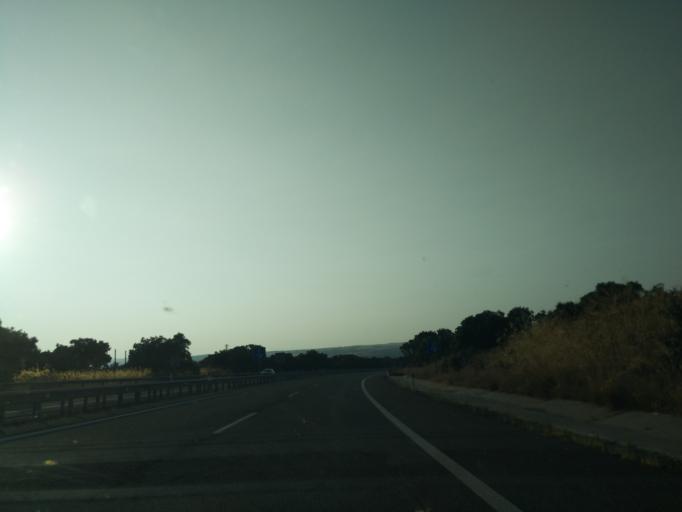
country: ES
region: Castille and Leon
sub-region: Provincia de Avila
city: Avila
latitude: 40.6719
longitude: -4.6767
